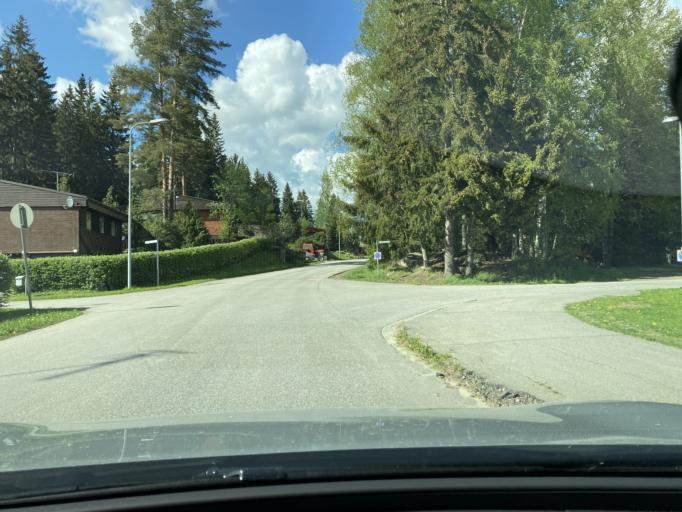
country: FI
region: Uusimaa
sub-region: Helsinki
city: Maentsaelae
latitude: 60.6477
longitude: 25.3171
